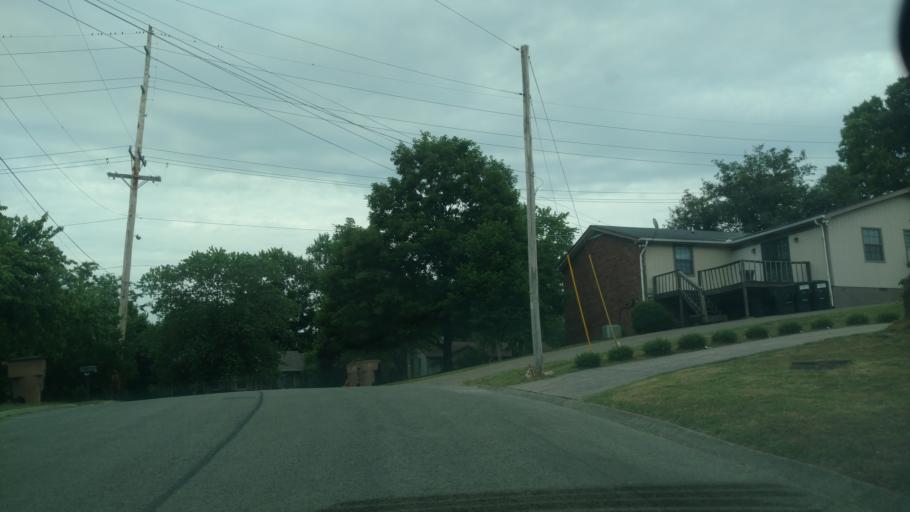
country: US
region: Tennessee
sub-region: Davidson County
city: Nashville
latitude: 36.1892
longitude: -86.7098
